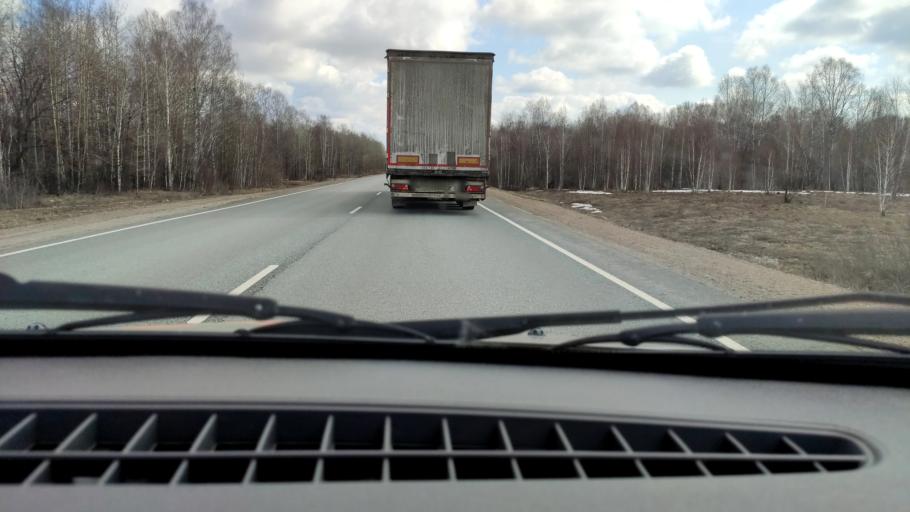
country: RU
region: Bashkortostan
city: Kudeyevskiy
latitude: 54.8170
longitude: 56.7734
